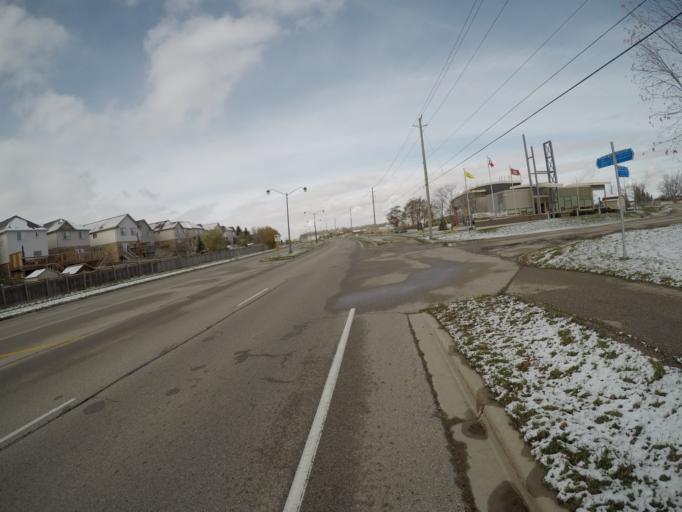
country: CA
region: Ontario
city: Waterloo
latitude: 43.5136
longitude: -80.4981
